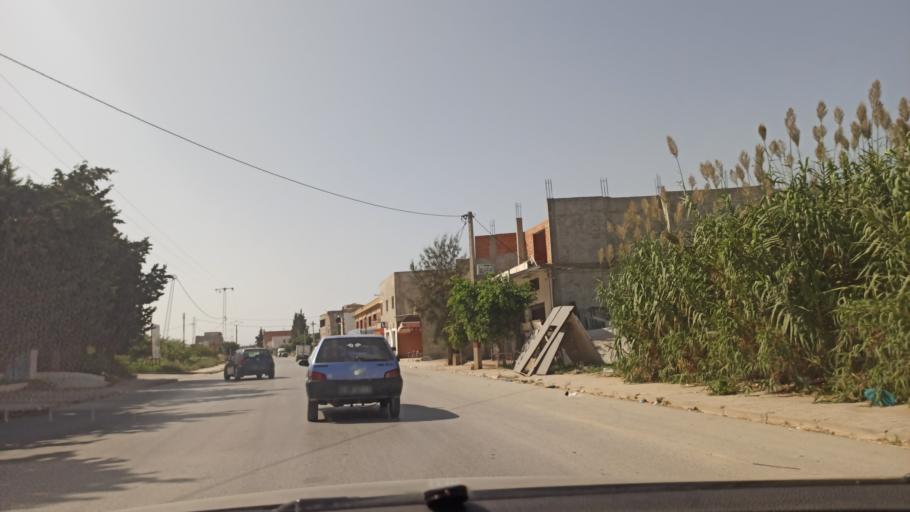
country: TN
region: Manouba
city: Manouba
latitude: 36.7572
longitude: 10.1038
